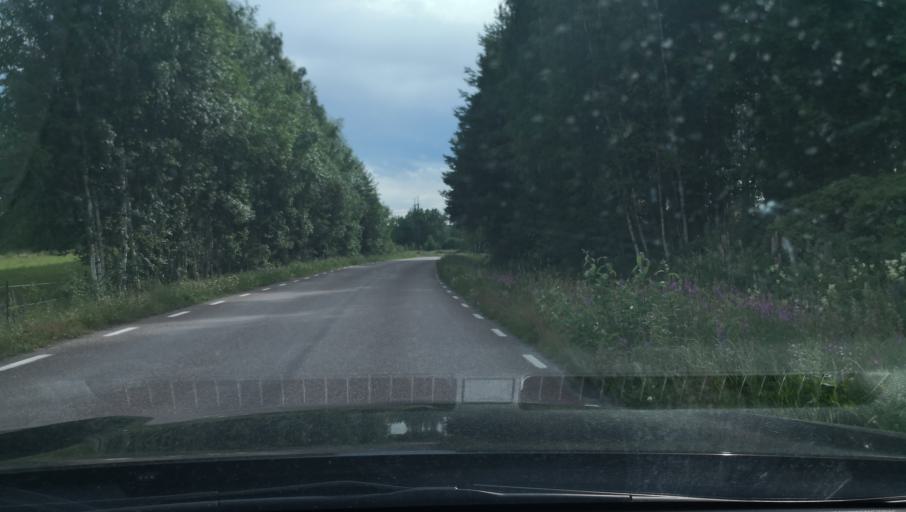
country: SE
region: Dalarna
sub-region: Smedjebackens Kommun
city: Smedjebacken
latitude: 60.0485
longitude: 15.5502
